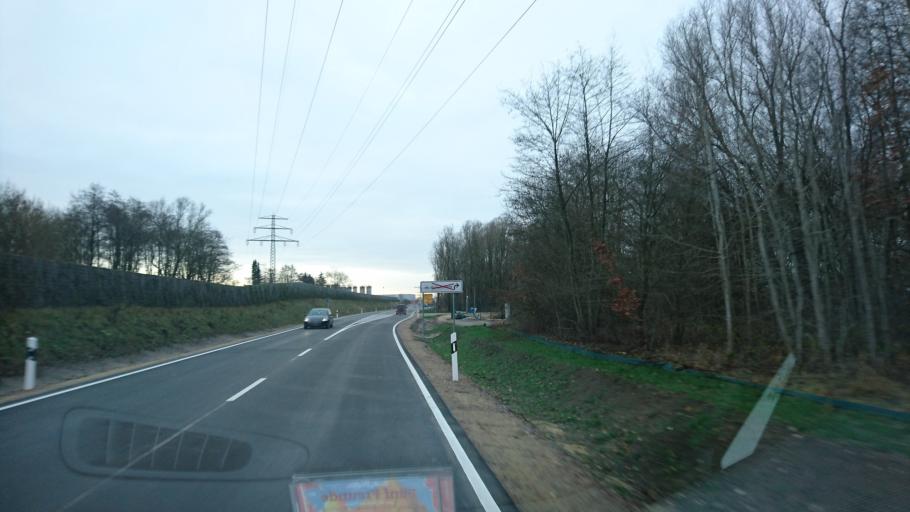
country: DE
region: Schleswig-Holstein
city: Pinneberg
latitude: 53.6727
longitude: 9.7822
